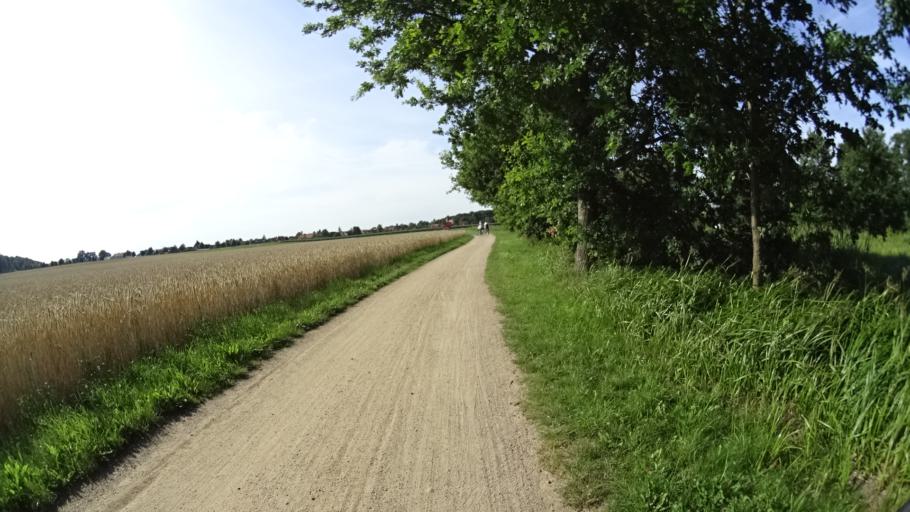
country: DE
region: Lower Saxony
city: Bardowick
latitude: 53.2857
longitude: 10.4032
